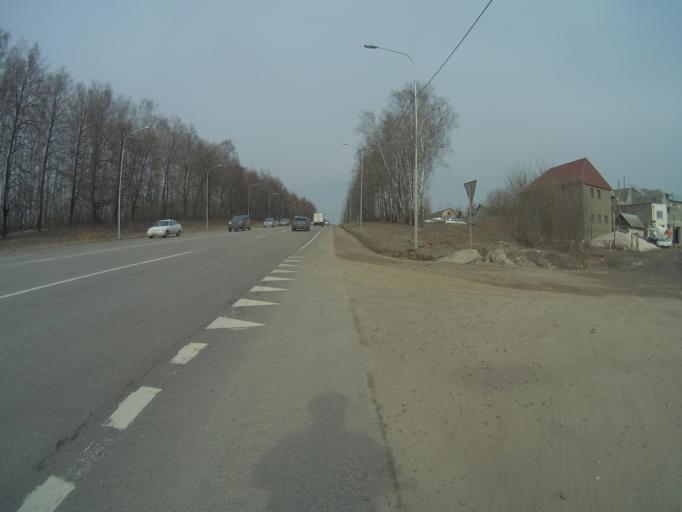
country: RU
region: Vladimir
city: Bogolyubovo
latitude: 56.1831
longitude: 40.5117
